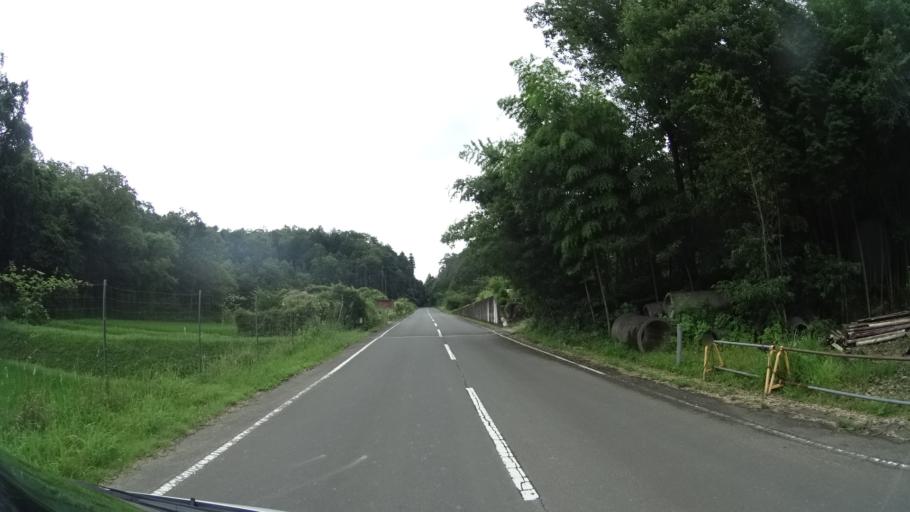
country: JP
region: Kyoto
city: Kameoka
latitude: 35.0917
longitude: 135.4316
